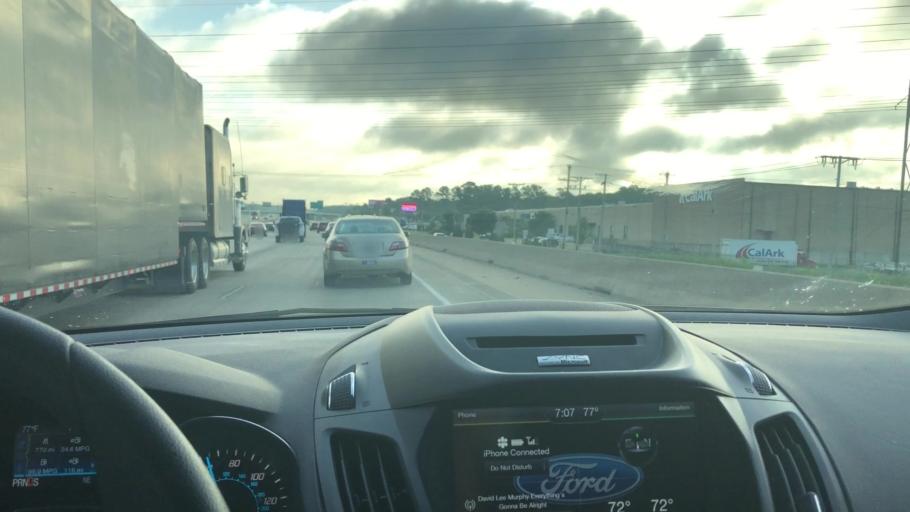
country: US
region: Arkansas
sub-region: Pulaski County
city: Alexander
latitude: 34.6500
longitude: -92.4163
